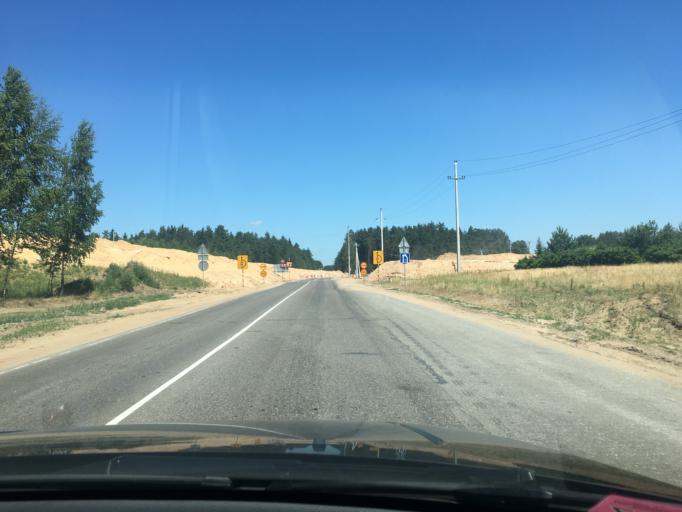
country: BY
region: Grodnenskaya
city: Iwye
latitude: 53.8838
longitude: 25.7408
